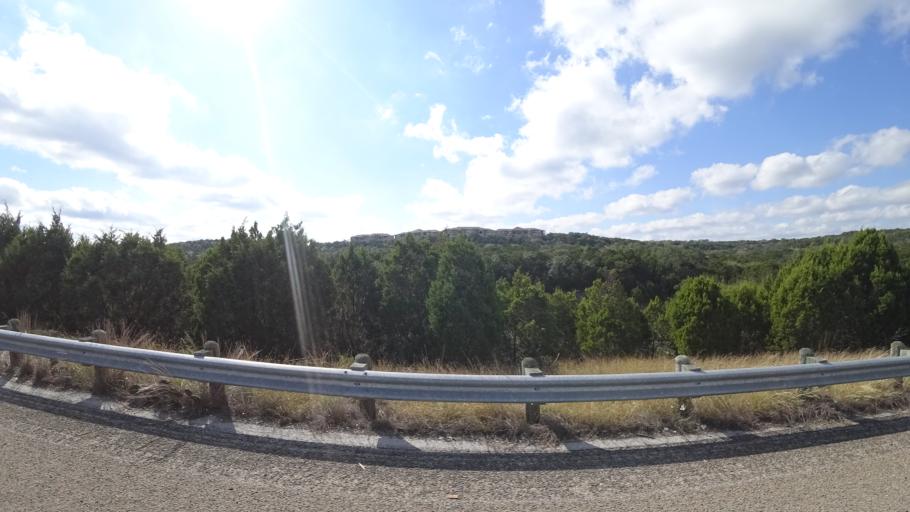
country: US
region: Texas
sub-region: Travis County
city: Barton Creek
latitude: 30.2624
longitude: -97.8899
